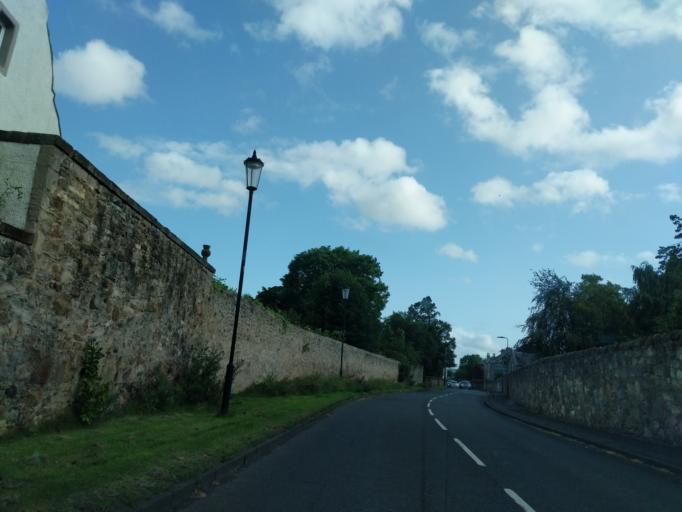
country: GB
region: Scotland
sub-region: East Lothian
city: Musselburgh
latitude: 55.9349
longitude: -3.0432
